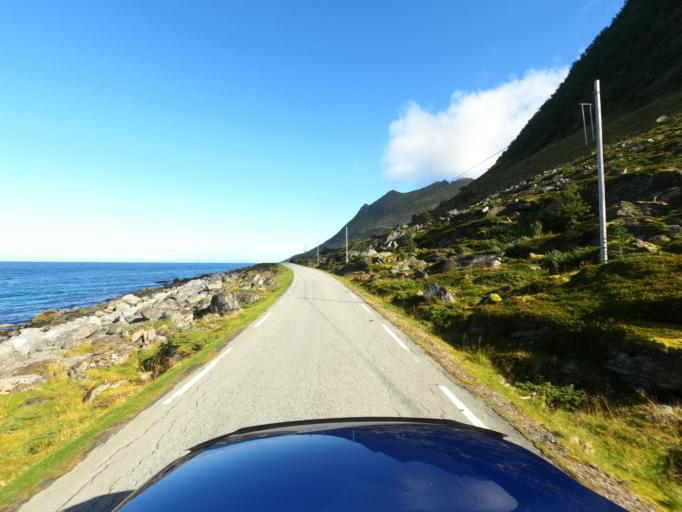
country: NO
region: Nordland
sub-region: Vagan
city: Kabelvag
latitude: 68.3209
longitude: 14.3120
